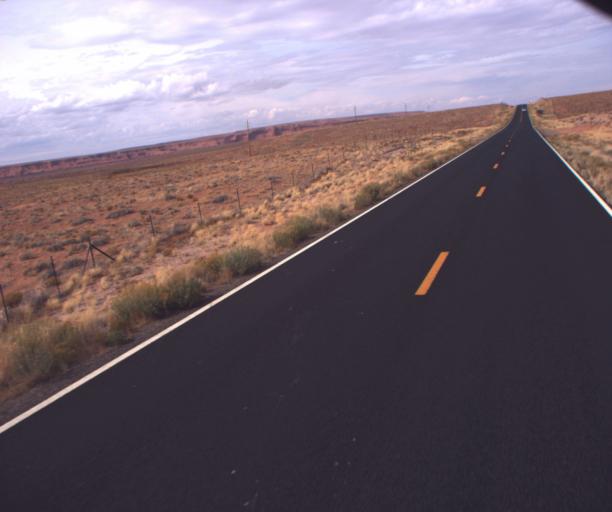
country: US
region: Arizona
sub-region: Apache County
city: Many Farms
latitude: 36.5783
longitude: -109.5530
